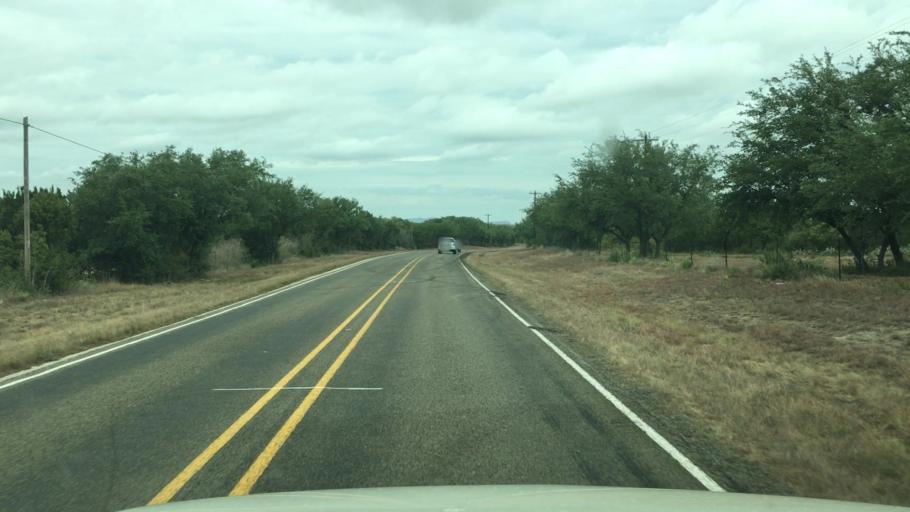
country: US
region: Texas
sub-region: Llano County
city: Horseshoe Bay
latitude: 30.4718
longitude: -98.4150
